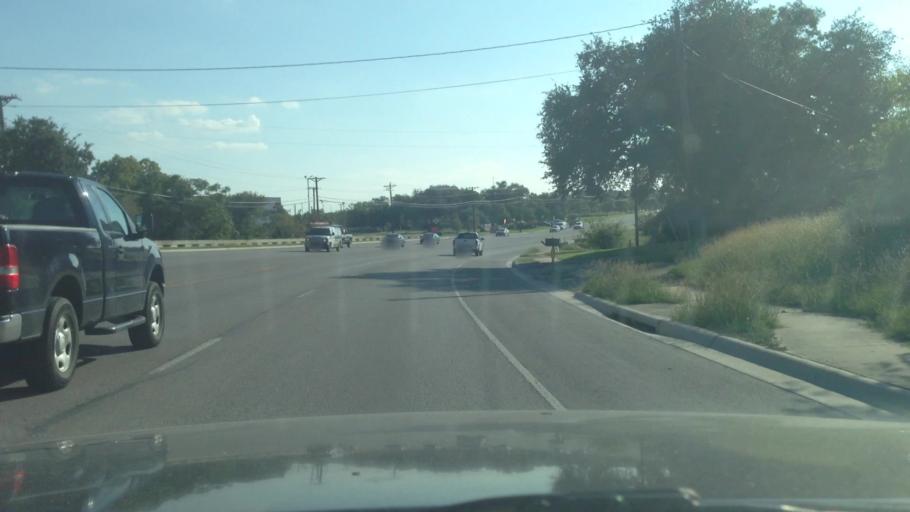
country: US
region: Texas
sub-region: Hays County
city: San Marcos
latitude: 29.8623
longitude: -97.9647
